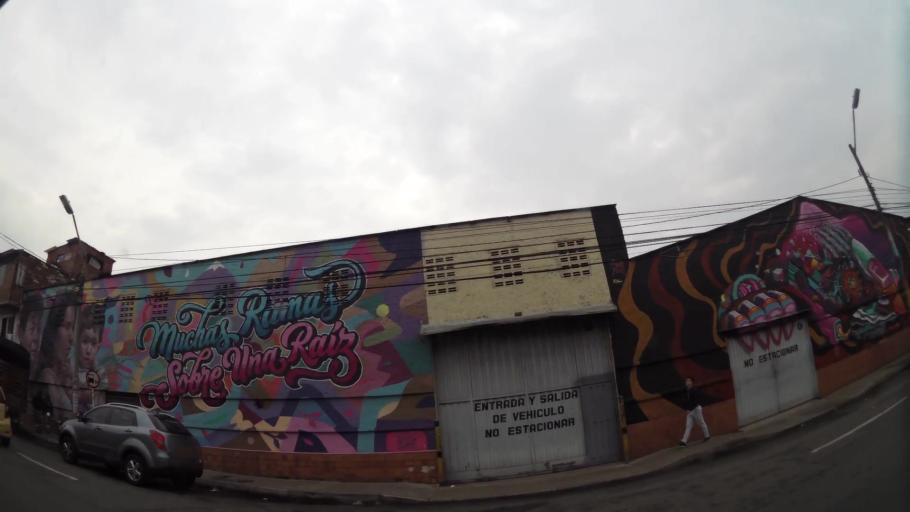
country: CO
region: Antioquia
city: Medellin
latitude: 6.2270
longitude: -75.5729
